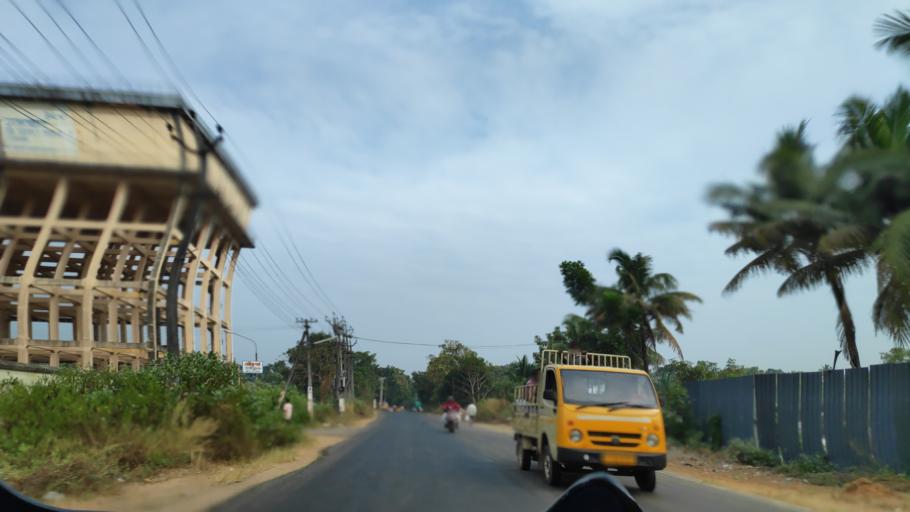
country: IN
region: Kerala
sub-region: Kottayam
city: Vaikam
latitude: 9.7599
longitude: 76.3625
